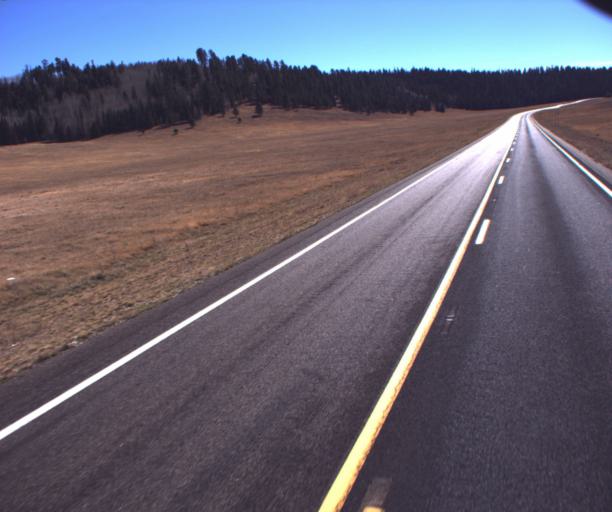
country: US
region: Arizona
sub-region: Coconino County
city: Grand Canyon
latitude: 36.4810
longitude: -112.1273
